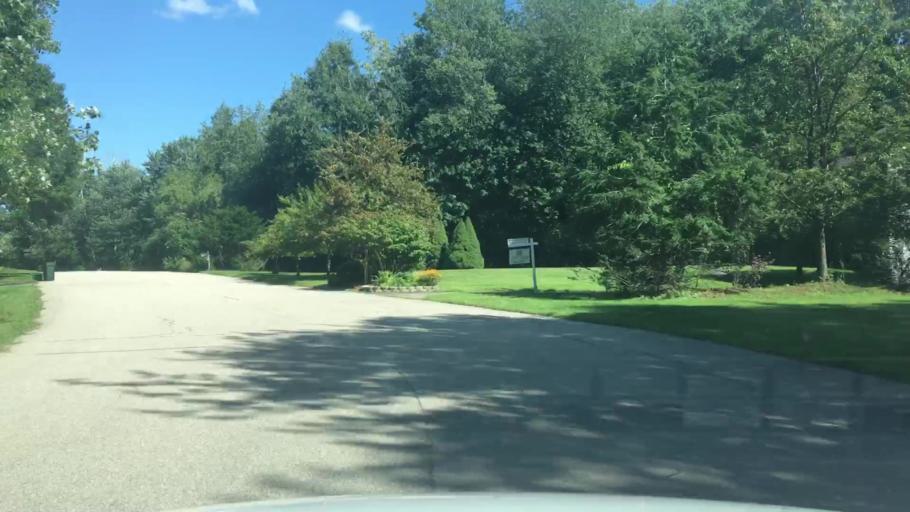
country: US
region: Maine
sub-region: York County
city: Eliot
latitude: 43.1693
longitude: -70.8351
